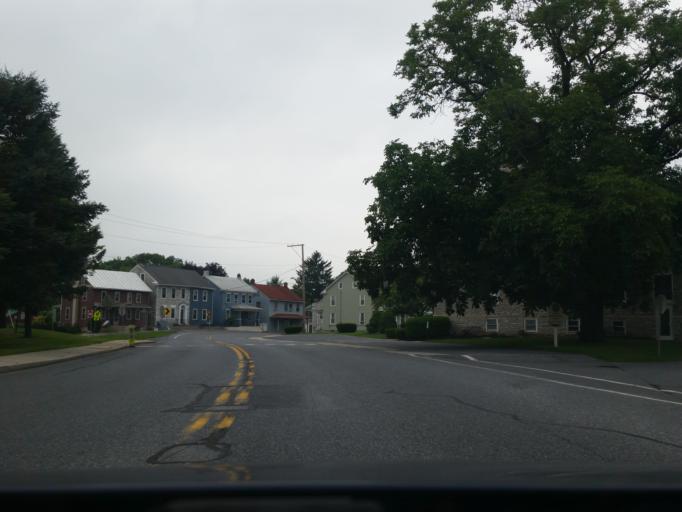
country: US
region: Pennsylvania
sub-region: Lebanon County
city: Annville
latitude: 40.3272
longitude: -76.5140
